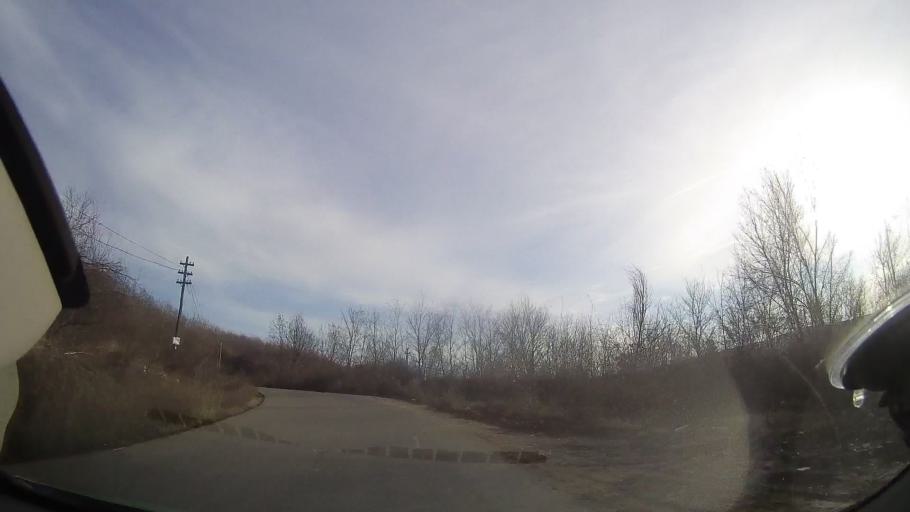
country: RO
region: Bihor
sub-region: Comuna Sarbi
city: Sarbi
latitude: 47.1872
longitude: 22.1273
